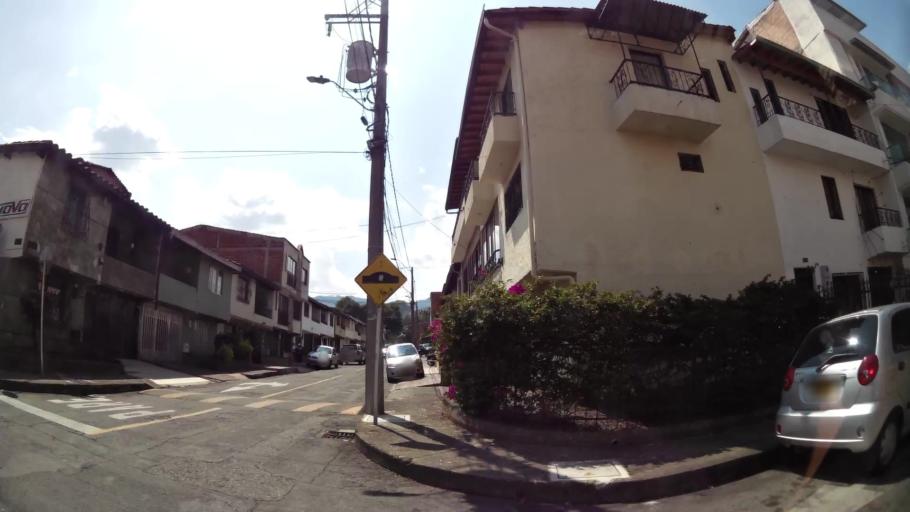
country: CO
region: Antioquia
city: Itagui
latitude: 6.2243
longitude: -75.6027
